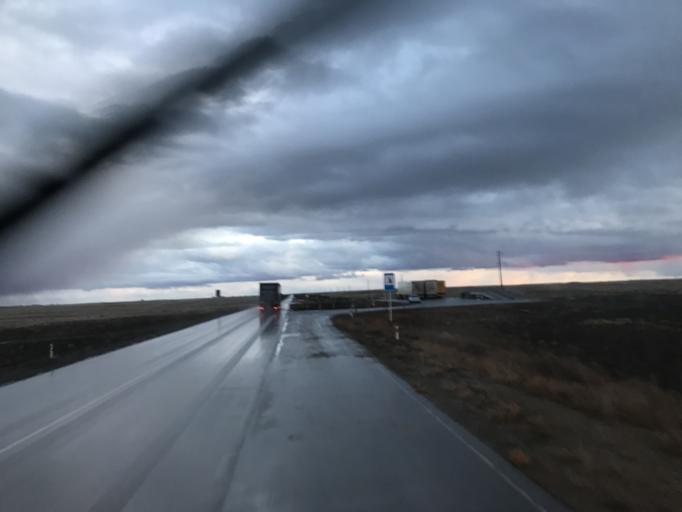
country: KZ
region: Qostanay
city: Ordzhonikidze
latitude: 52.4481
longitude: 61.7718
